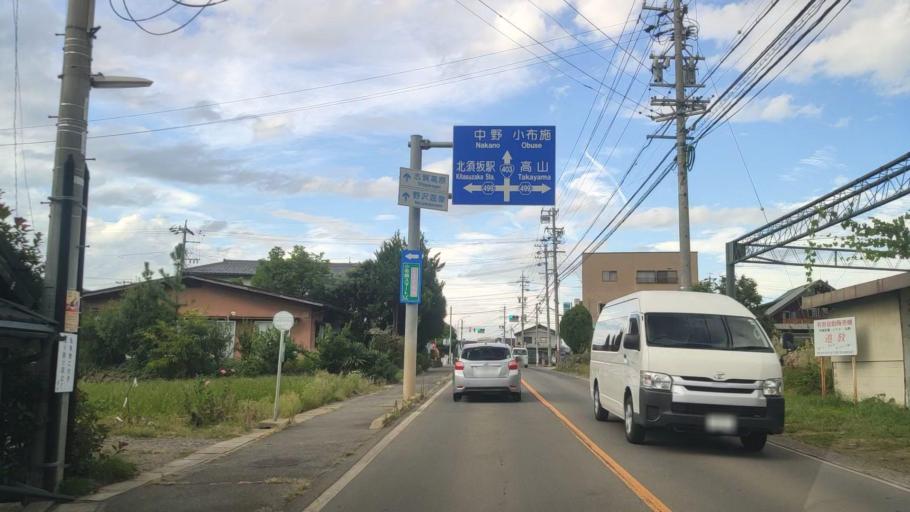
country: JP
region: Nagano
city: Suzaka
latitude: 36.6773
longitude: 138.3175
